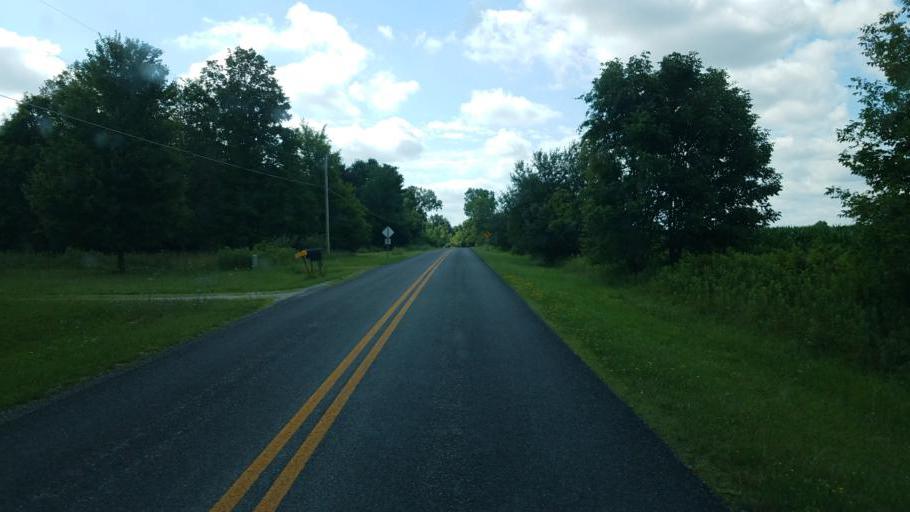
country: US
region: Ohio
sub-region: Delaware County
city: Ashley
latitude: 40.3111
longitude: -82.9463
